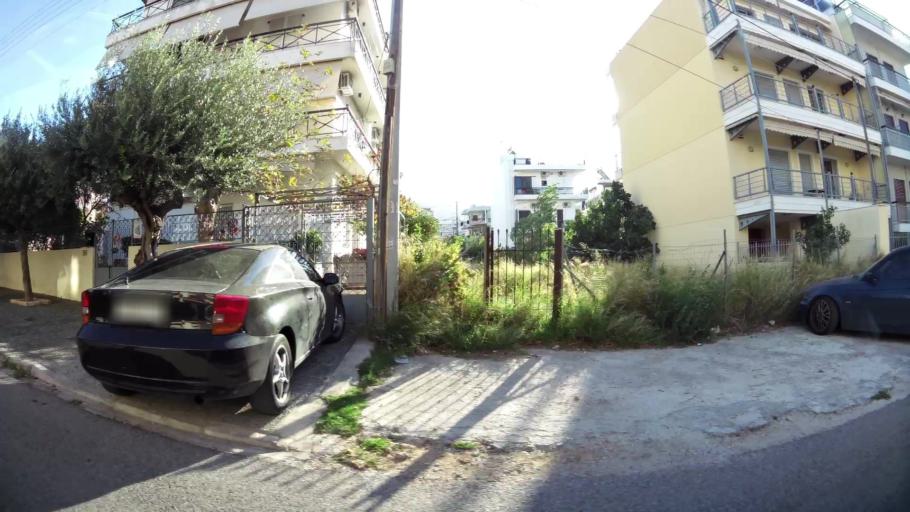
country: GR
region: Attica
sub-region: Nomarchia Athinas
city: Elliniko
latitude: 37.8799
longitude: 23.7504
